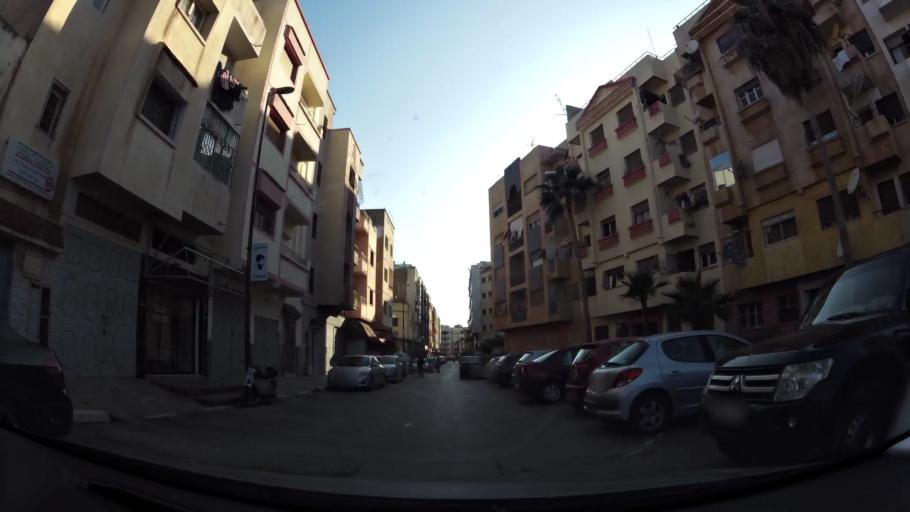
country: MA
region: Rabat-Sale-Zemmour-Zaer
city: Sale
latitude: 34.0554
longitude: -6.7917
